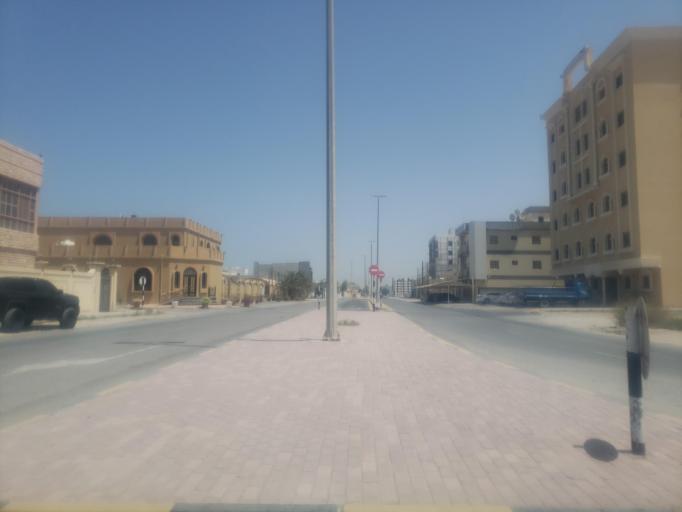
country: AE
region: Ra's al Khaymah
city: Ras al-Khaimah
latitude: 25.8082
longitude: 55.9587
